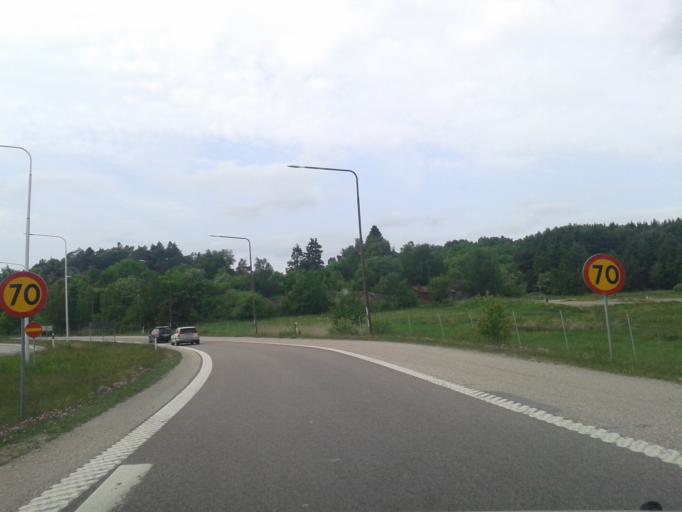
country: SE
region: Vaestra Goetaland
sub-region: Kungalvs Kommun
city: Kungalv
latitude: 57.8759
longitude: 11.9662
